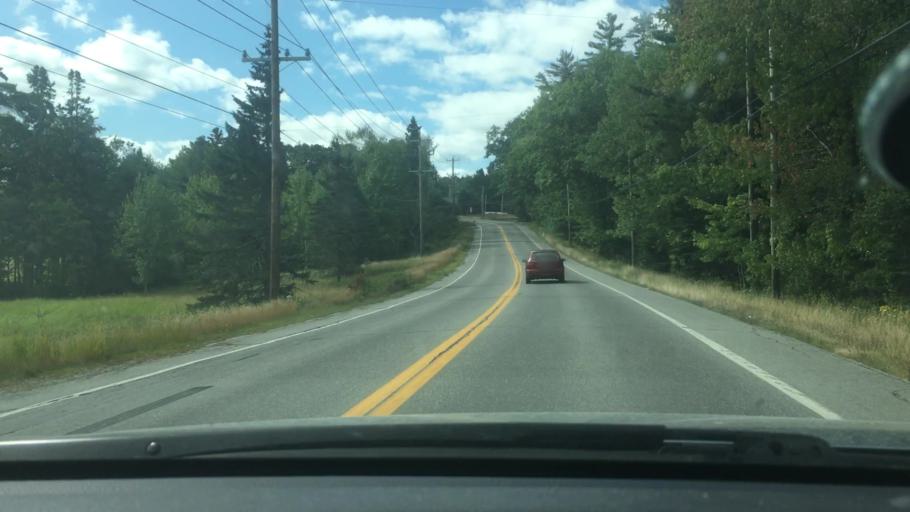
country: US
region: Maine
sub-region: Hancock County
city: Trenton
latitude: 44.3762
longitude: -68.3317
